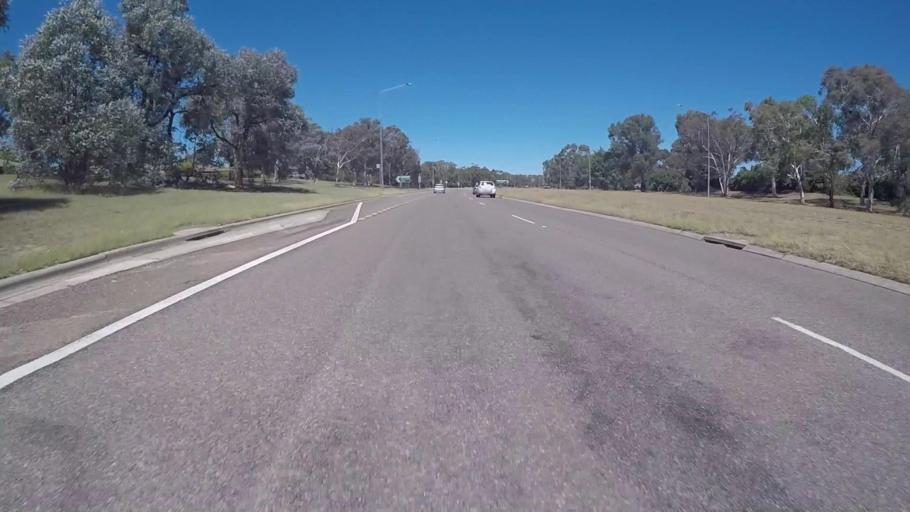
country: AU
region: Australian Capital Territory
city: Macarthur
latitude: -35.4010
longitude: 149.0745
